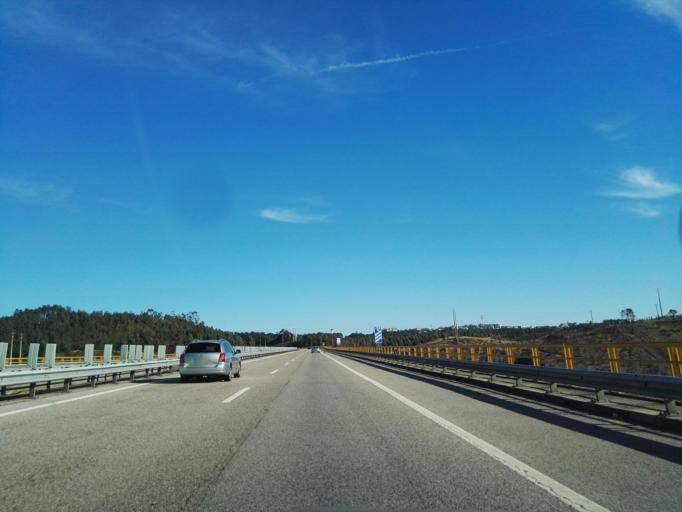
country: PT
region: Santarem
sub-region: Abrantes
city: Tramagal
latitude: 39.4804
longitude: -8.2352
